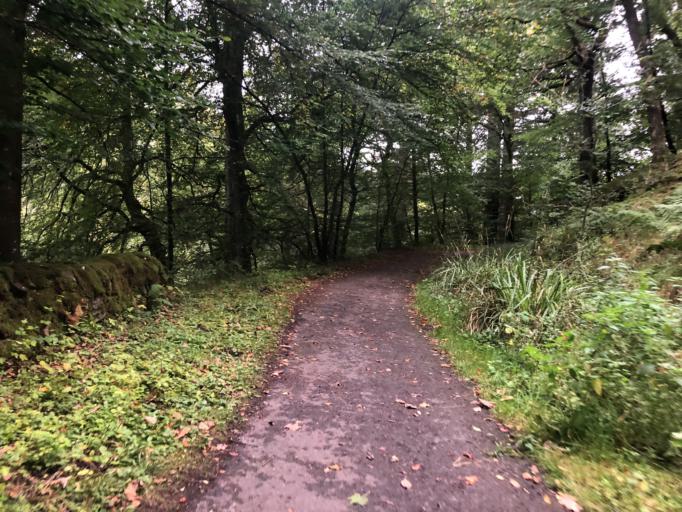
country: GB
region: Scotland
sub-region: Perth and Kinross
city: Pitlochry
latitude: 56.7291
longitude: -3.7765
